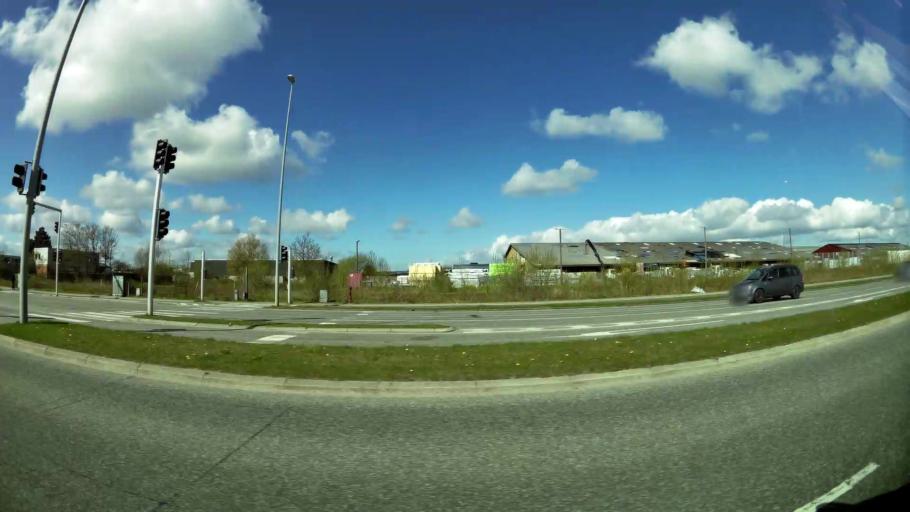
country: DK
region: North Denmark
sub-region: Alborg Kommune
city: Aalborg
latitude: 57.0357
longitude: 9.9311
